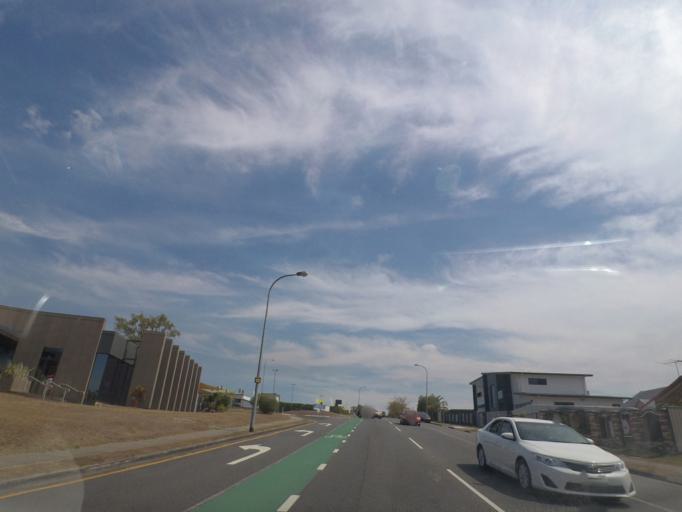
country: AU
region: Queensland
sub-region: Brisbane
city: Sunnybank Hills
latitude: -27.5956
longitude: 153.0650
